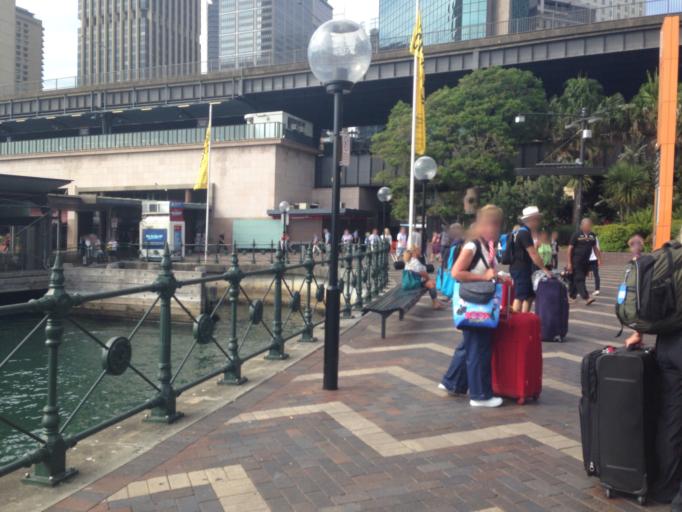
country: AU
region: New South Wales
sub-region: City of Sydney
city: Sydney
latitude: -33.8607
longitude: 151.2095
